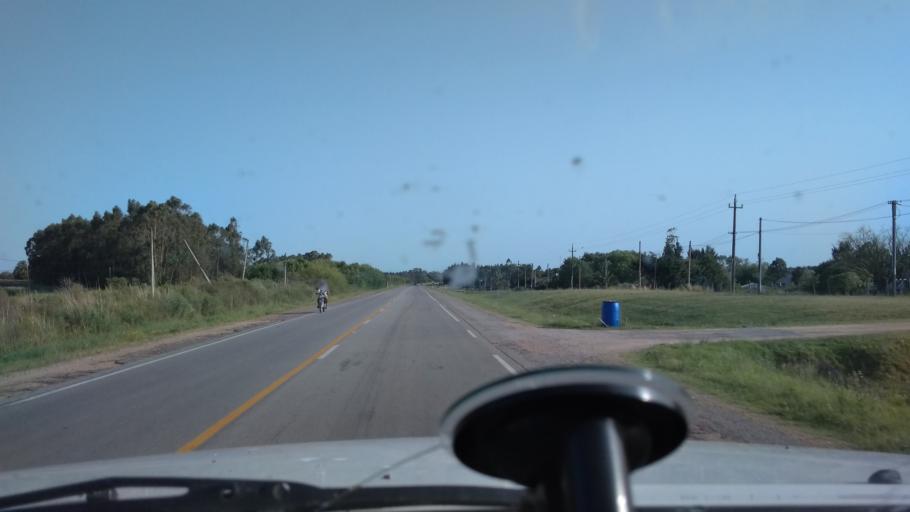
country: UY
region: Canelones
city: Santa Rosa
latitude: -34.5506
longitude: -56.0591
